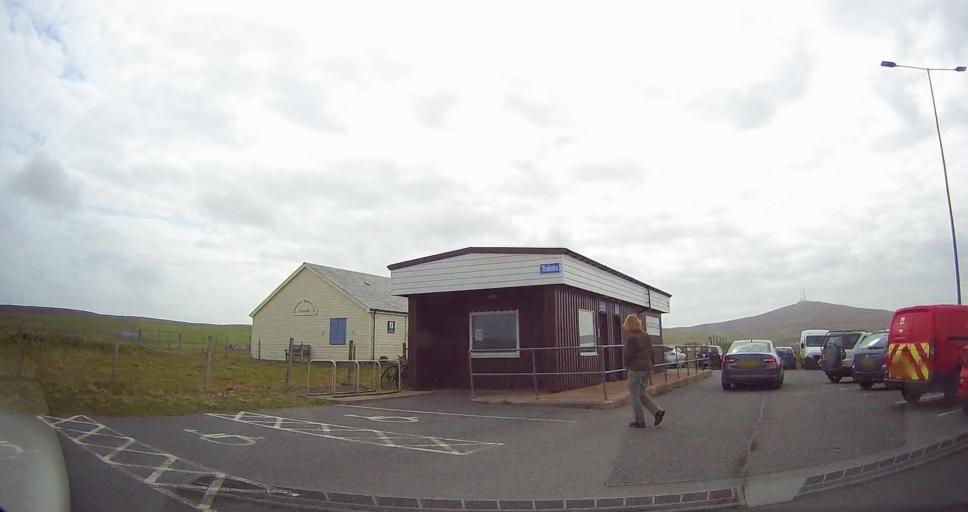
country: GB
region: Scotland
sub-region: Shetland Islands
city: Shetland
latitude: 60.1563
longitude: -1.1216
